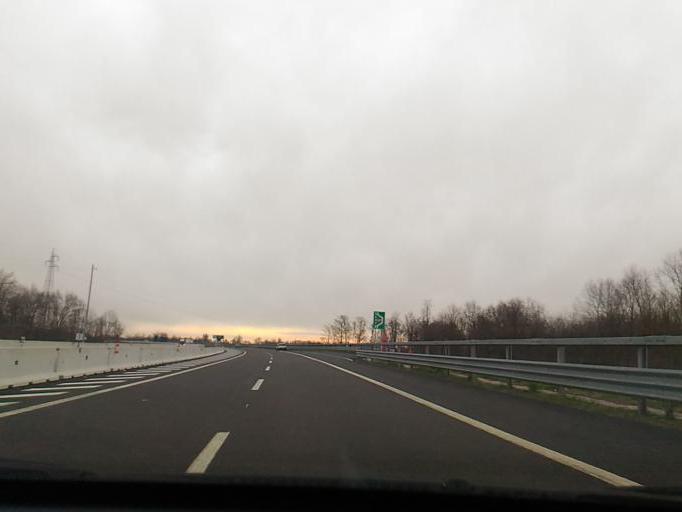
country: IT
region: Lombardy
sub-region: Provincia di Como
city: Mozzate
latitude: 45.6616
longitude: 8.9463
